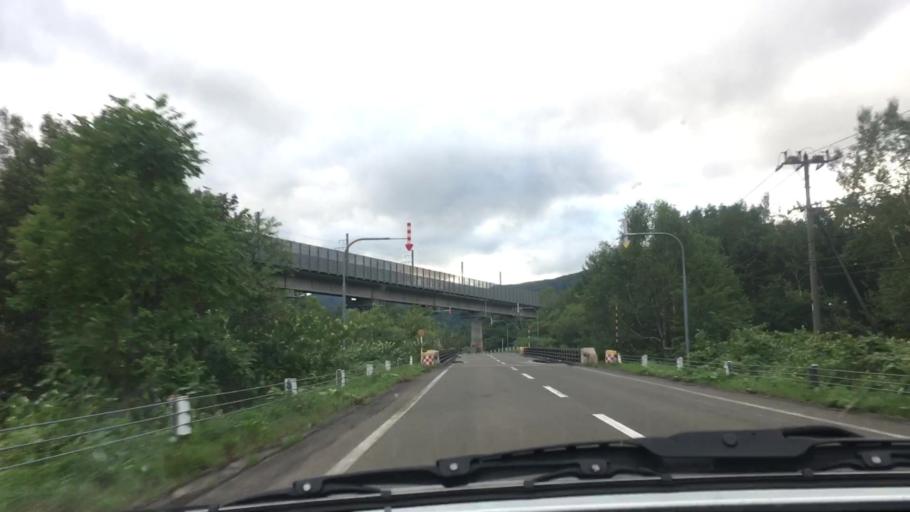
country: JP
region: Hokkaido
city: Shimo-furano
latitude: 43.0590
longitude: 142.5645
